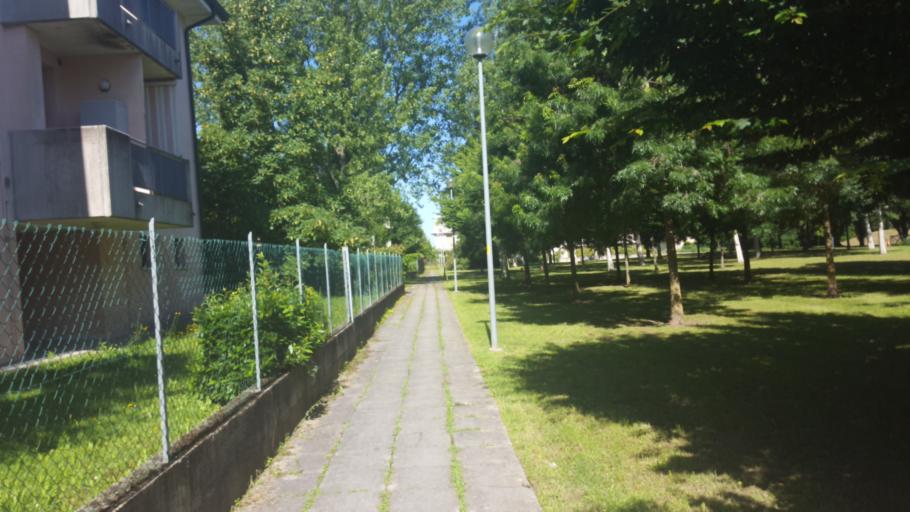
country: IT
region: Veneto
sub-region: Provincia di Venezia
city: San Dona di Piave
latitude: 45.6370
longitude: 12.5712
